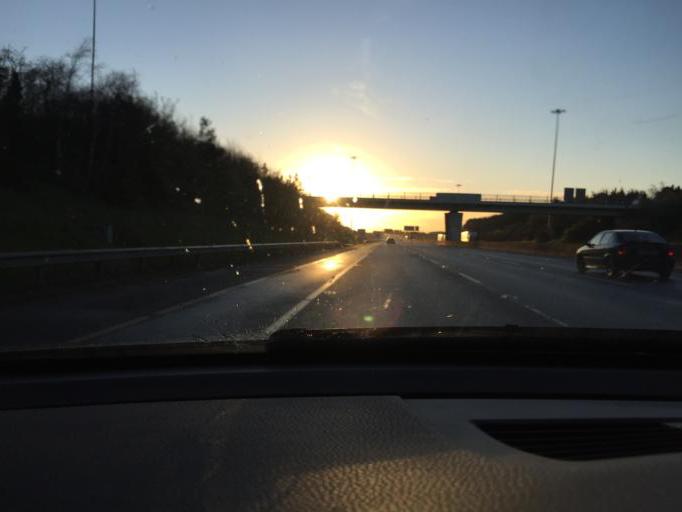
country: IE
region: Leinster
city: Ballymun
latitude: 53.4092
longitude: -6.2668
